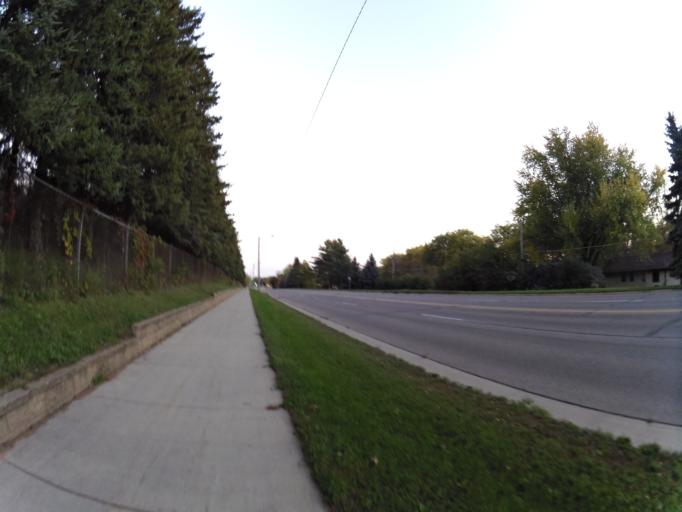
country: US
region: Minnesota
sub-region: Olmsted County
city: Rochester
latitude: 44.0393
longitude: -92.4837
